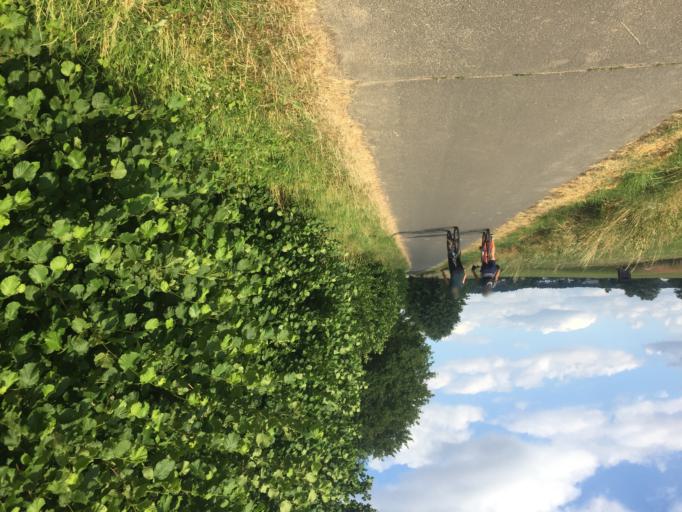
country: DE
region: Hesse
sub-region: Regierungsbezirk Giessen
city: Heuchelheim
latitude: 50.6314
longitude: 8.5897
